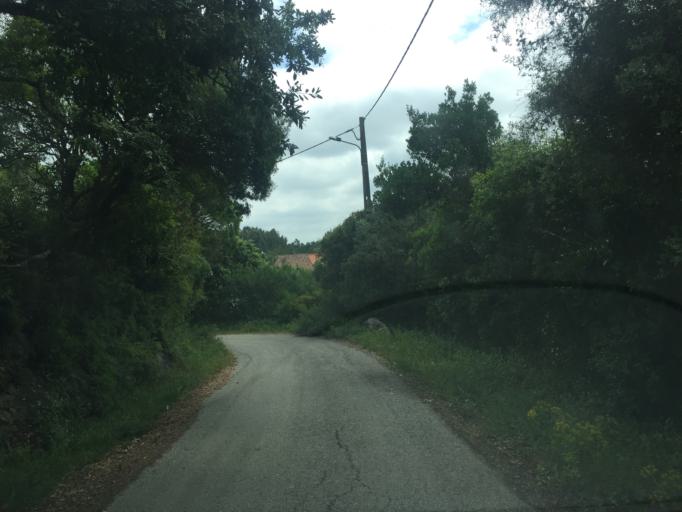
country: PT
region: Coimbra
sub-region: Figueira da Foz
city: Tavarede
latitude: 40.1861
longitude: -8.8258
